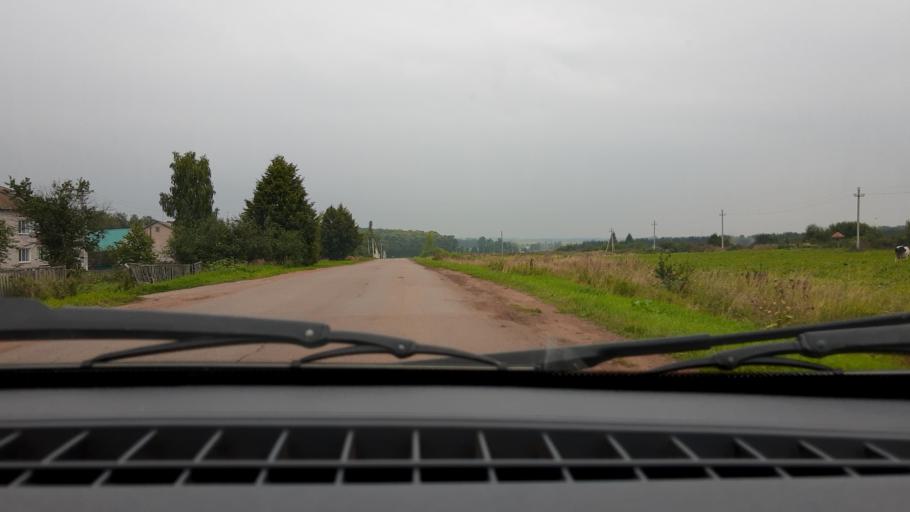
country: RU
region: Bashkortostan
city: Avdon
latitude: 54.7861
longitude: 55.7602
